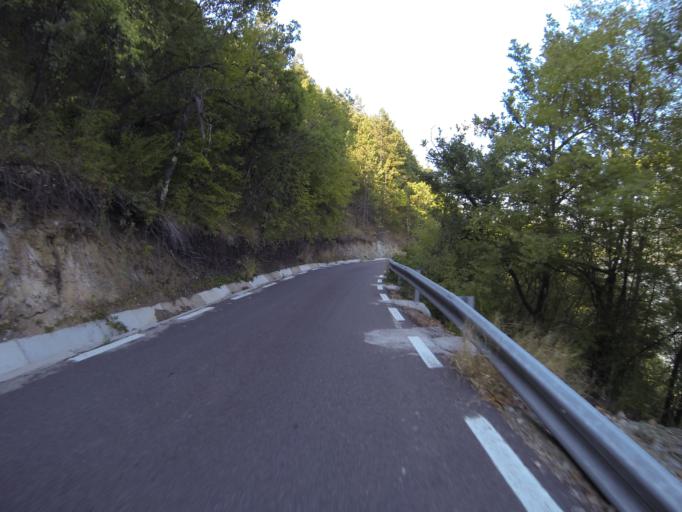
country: RO
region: Mehedinti
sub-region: Comuna Dubova
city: Dubova
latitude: 44.5403
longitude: 22.2092
